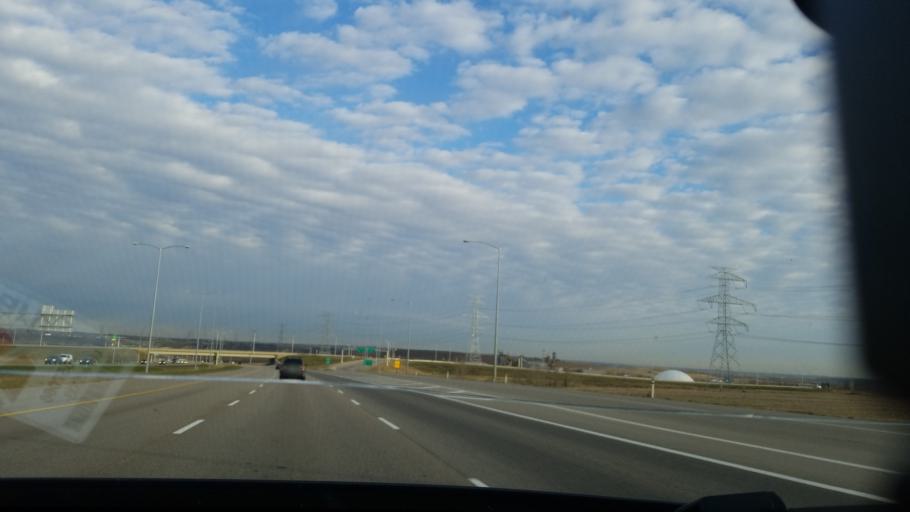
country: CA
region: Alberta
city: Sherwood Park
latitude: 53.5822
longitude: -113.3442
